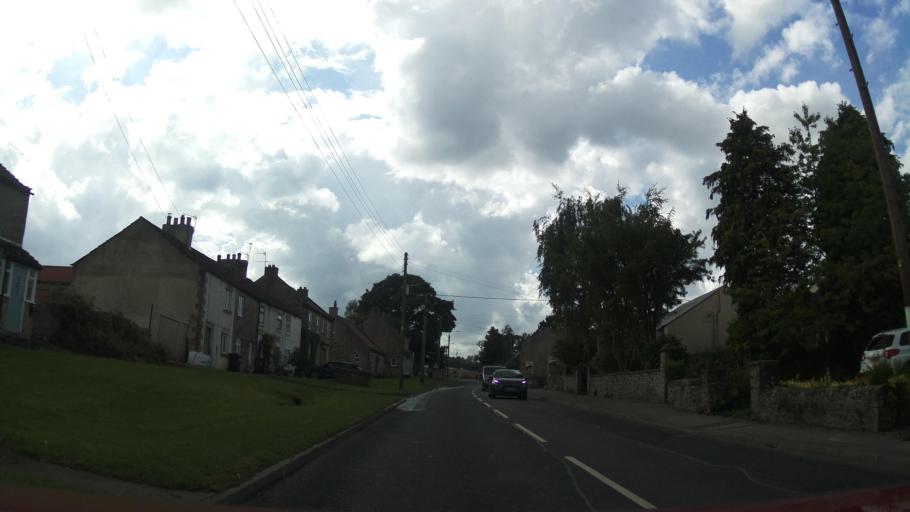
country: GB
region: England
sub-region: North Yorkshire
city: Catterick Garrison
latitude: 54.4184
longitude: -1.6929
